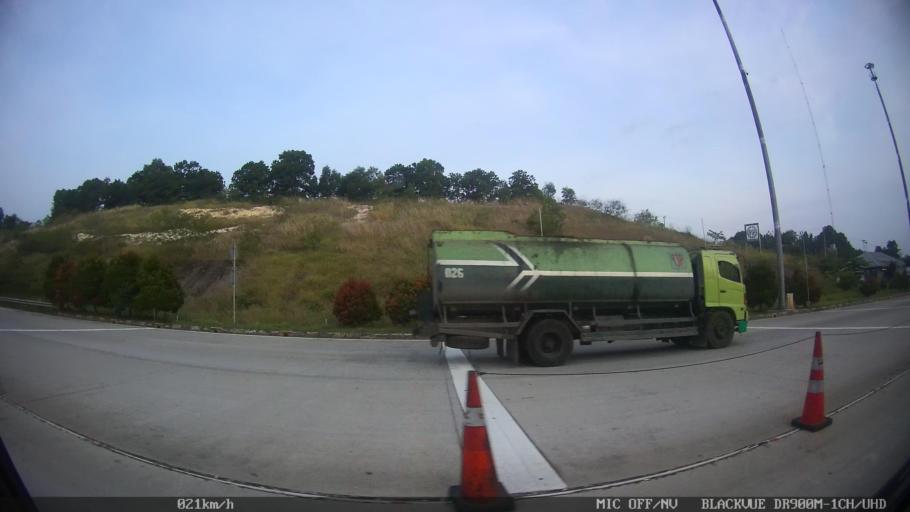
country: ID
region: Lampung
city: Penengahan
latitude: -5.8420
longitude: 105.7283
